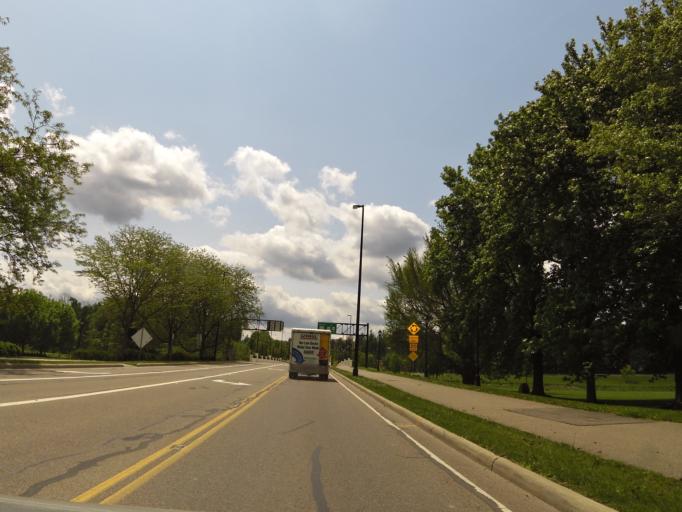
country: US
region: Ohio
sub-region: Athens County
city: Athens
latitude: 39.3218
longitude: -82.1048
